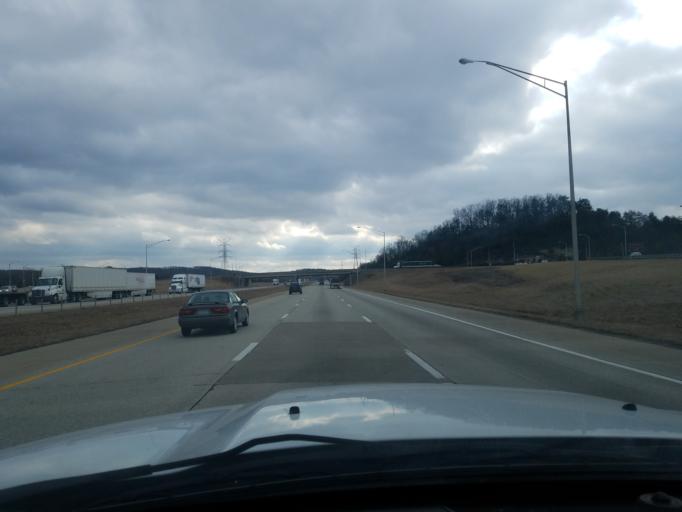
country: US
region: Kentucky
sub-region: Bullitt County
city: Shepherdsville
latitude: 37.9277
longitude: -85.6880
